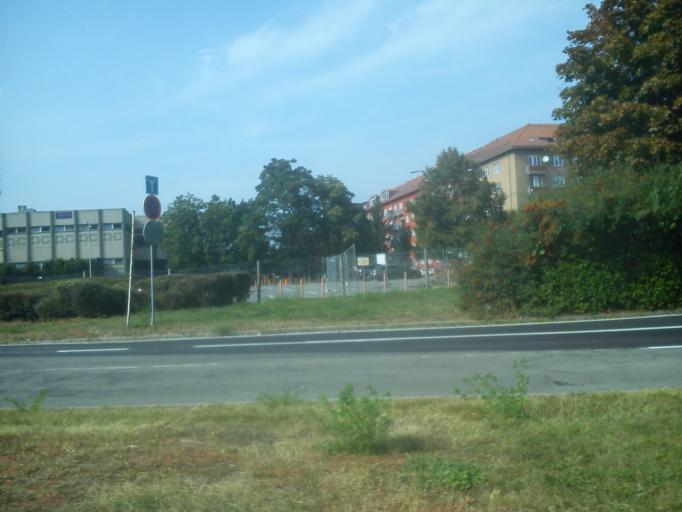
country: CZ
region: South Moravian
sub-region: Mesto Brno
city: Brno
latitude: 49.1850
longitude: 16.5869
